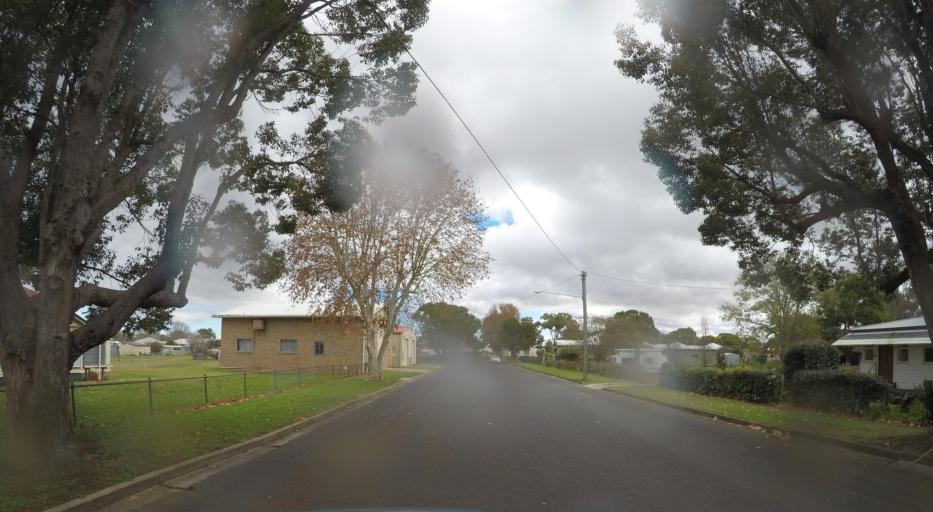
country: AU
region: Queensland
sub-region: Southern Downs
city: Warwick
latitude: -28.0347
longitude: 151.9852
